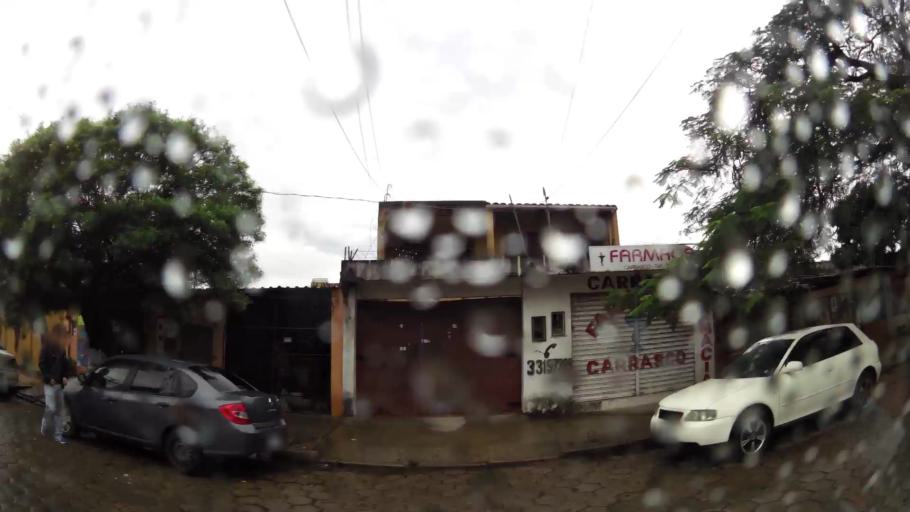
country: BO
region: Santa Cruz
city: Santa Cruz de la Sierra
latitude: -17.7786
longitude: -63.1671
